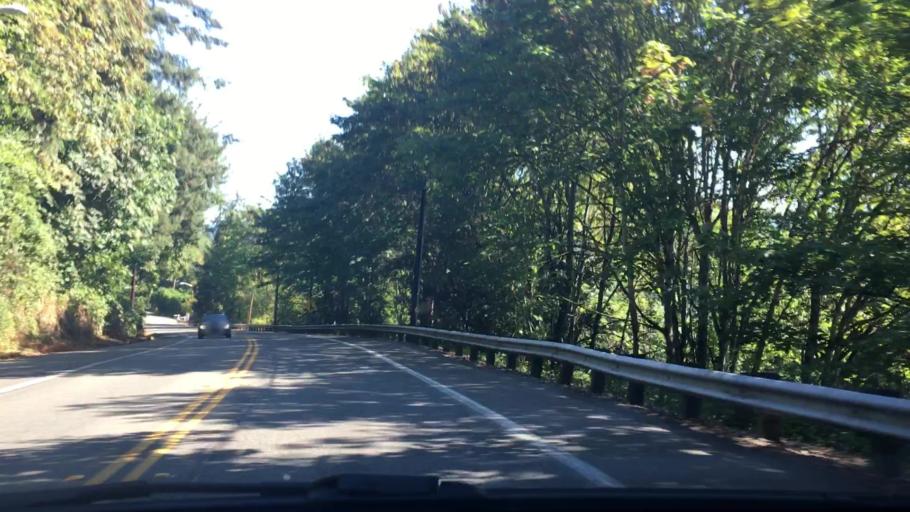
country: US
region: Washington
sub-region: King County
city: West Lake Sammamish
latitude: 47.5895
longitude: -122.0849
